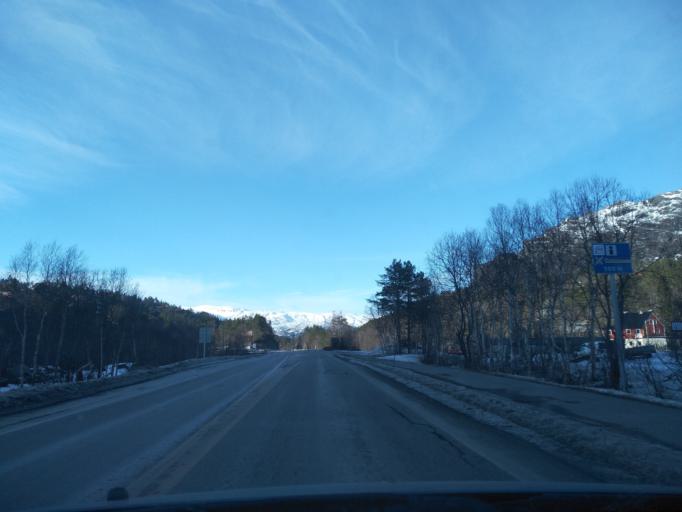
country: NO
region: Hordaland
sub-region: Odda
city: Odda
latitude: 59.9012
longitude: 6.6247
